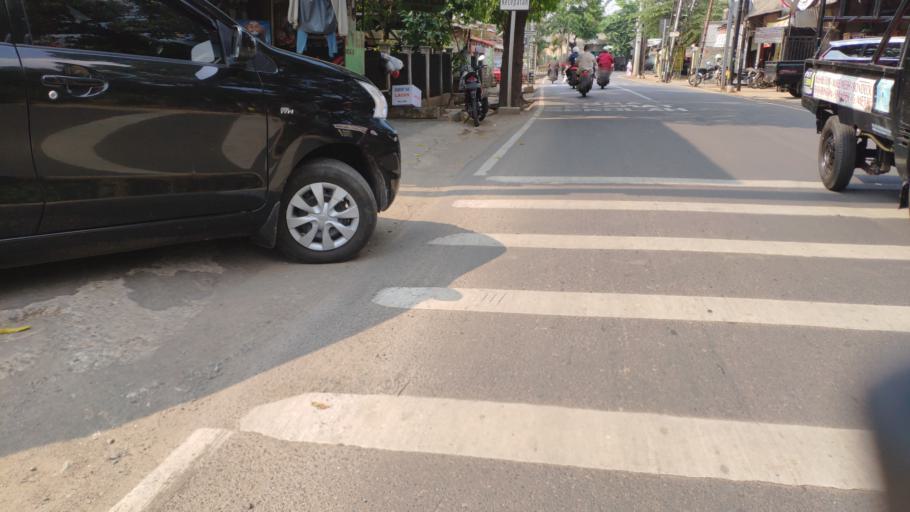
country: ID
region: West Java
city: Pamulang
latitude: -6.3204
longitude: 106.8108
